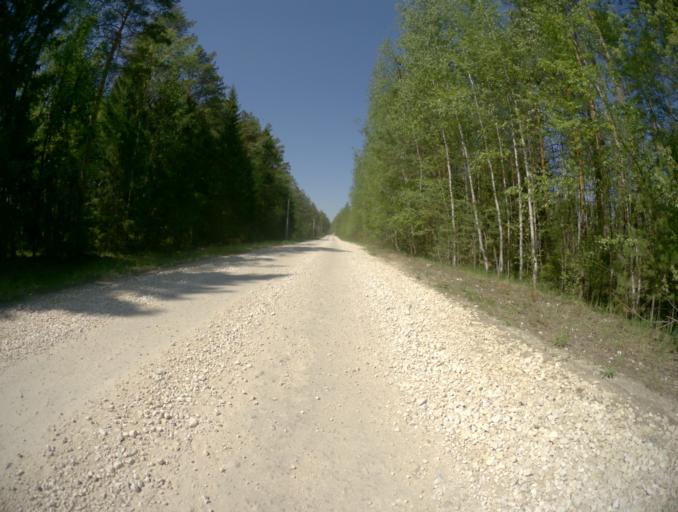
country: RU
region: Vladimir
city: Gusevskiy
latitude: 55.7209
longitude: 40.5856
